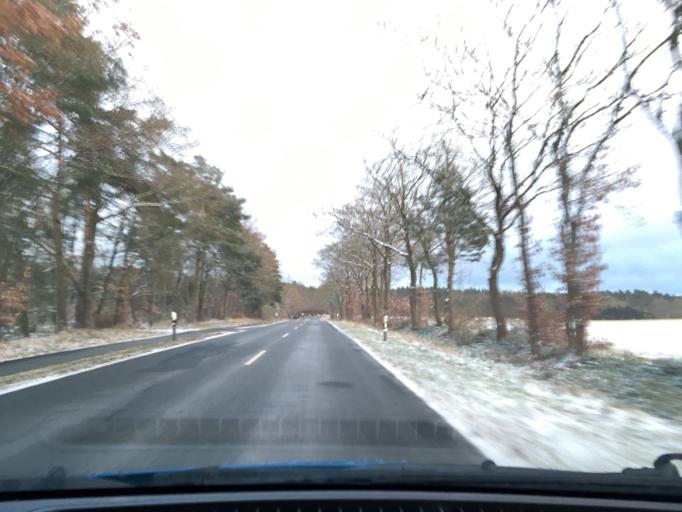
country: DE
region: Lower Saxony
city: Sudergellersen
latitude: 53.2233
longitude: 10.3243
